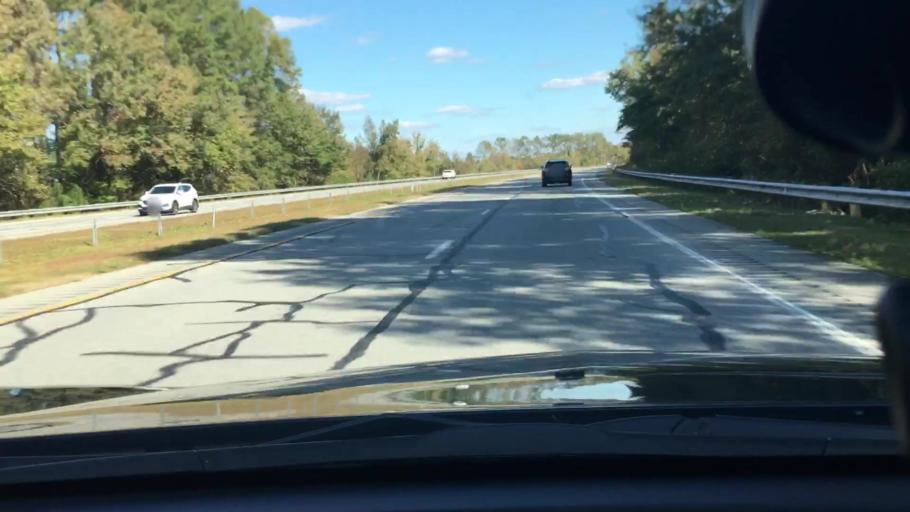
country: US
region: North Carolina
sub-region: Pitt County
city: Farmville
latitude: 35.6164
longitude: -77.6508
